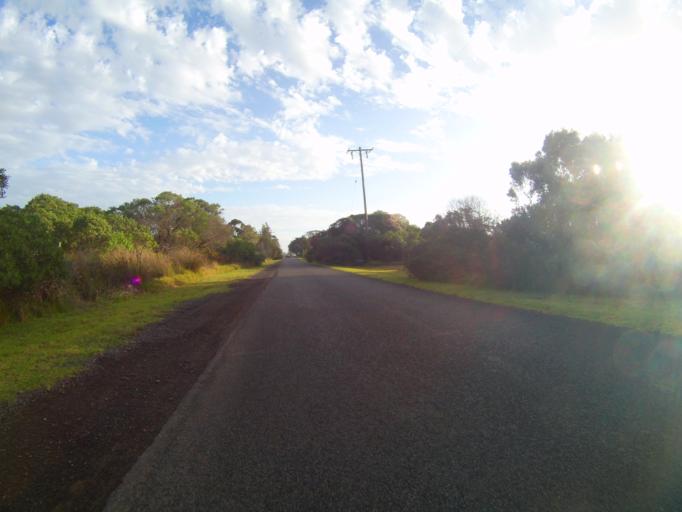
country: AU
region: Victoria
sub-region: Queenscliffe
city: Queenscliff
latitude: -38.2652
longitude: 144.6197
